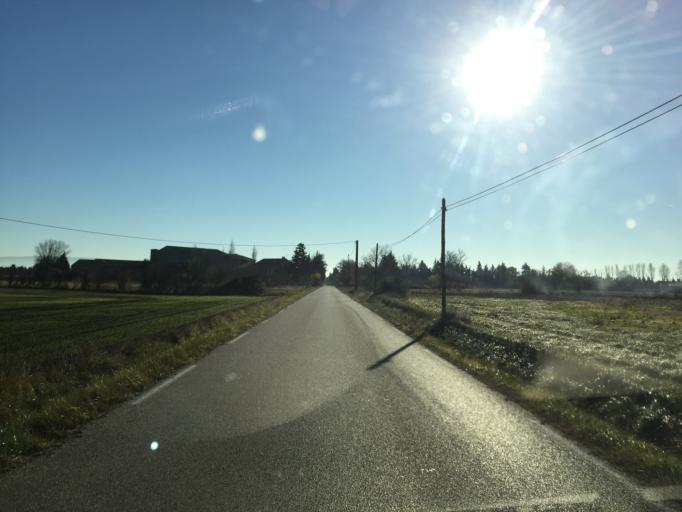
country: FR
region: Provence-Alpes-Cote d'Azur
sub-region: Departement du Vaucluse
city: Entraigues-sur-la-Sorgue
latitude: 44.0176
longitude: 4.9289
